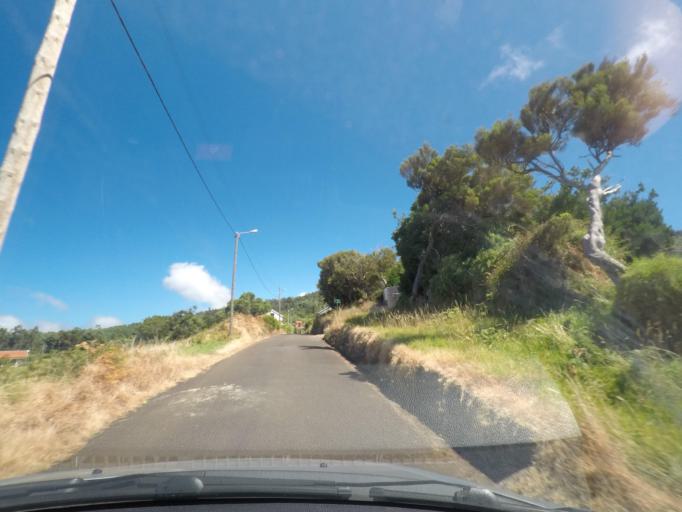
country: PT
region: Madeira
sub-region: Porto Moniz
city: Porto Moniz
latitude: 32.8431
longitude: -17.2097
